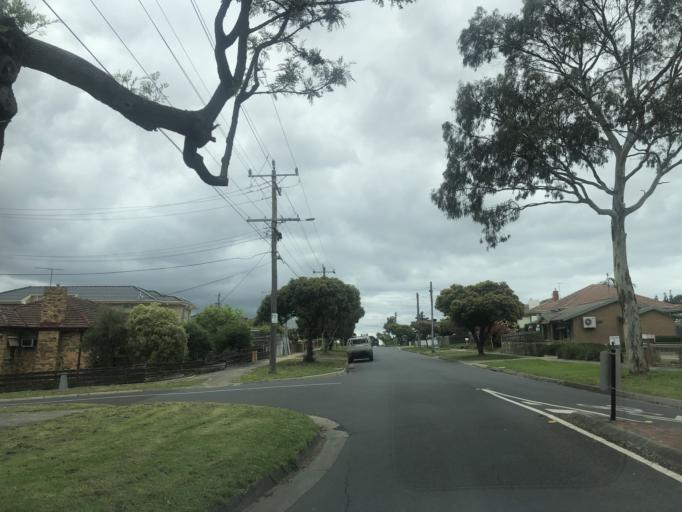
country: AU
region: Victoria
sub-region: Casey
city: Doveton
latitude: -37.9815
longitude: 145.2262
